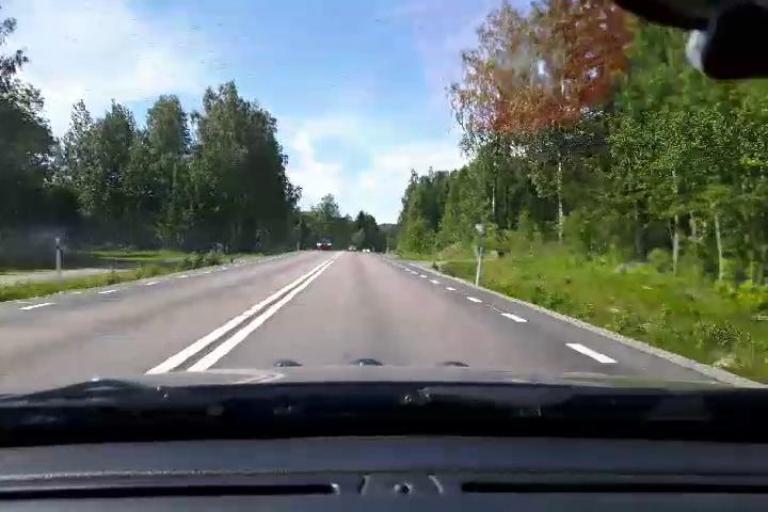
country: SE
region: Gaevleborg
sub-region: Bollnas Kommun
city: Kilafors
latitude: 61.1776
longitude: 16.7907
